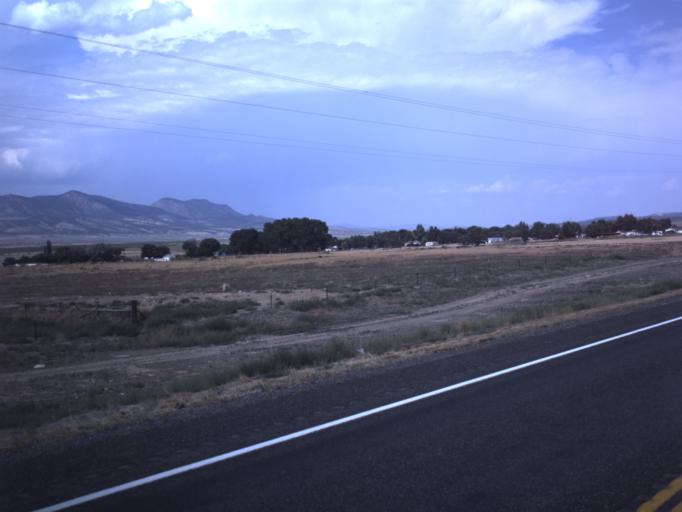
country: US
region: Utah
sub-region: Sanpete County
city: Gunnison
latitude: 39.2152
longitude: -111.8483
